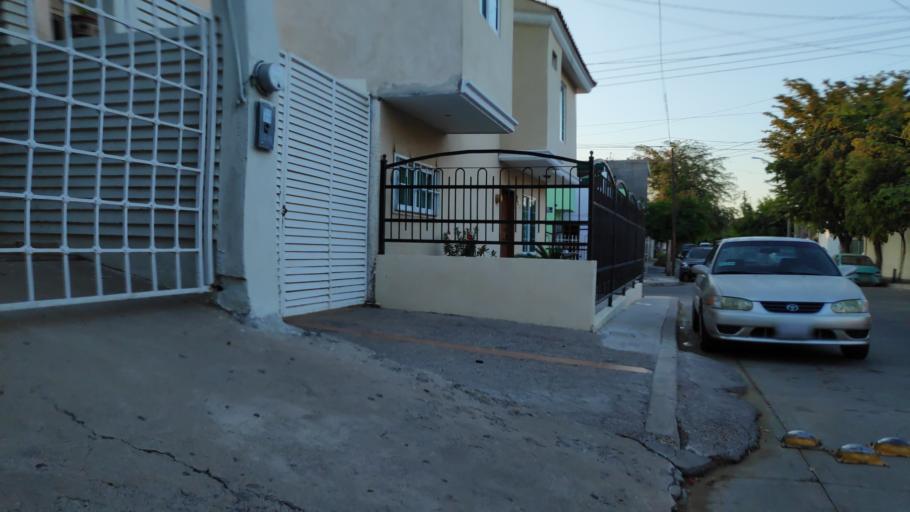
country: MX
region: Sinaloa
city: Culiacan
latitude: 24.7873
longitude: -107.4029
